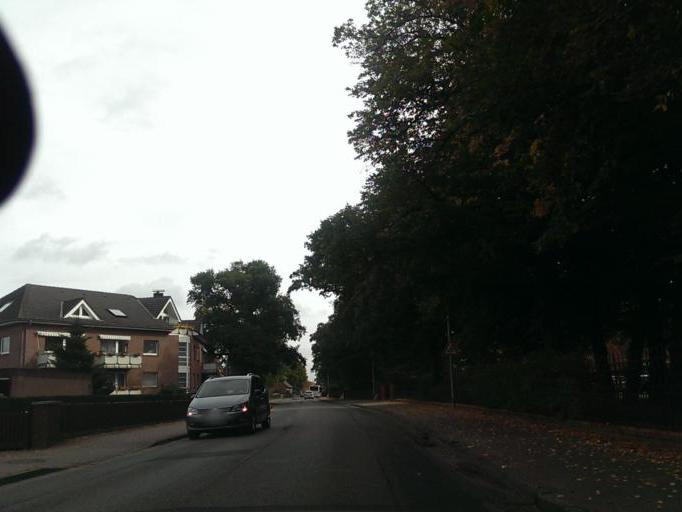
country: DE
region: Lower Saxony
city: Garbsen-Mitte
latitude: 52.4600
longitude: 9.5810
